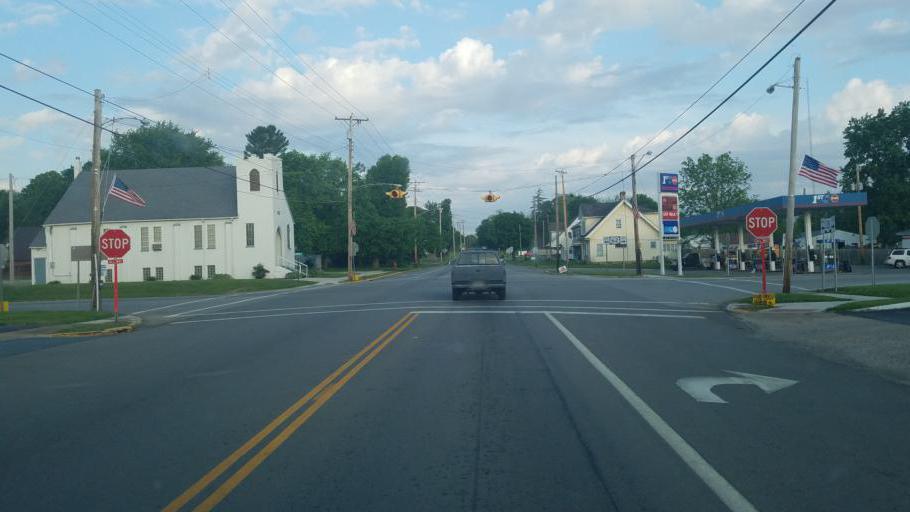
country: US
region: Ohio
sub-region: Highland County
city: Leesburg
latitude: 39.3457
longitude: -83.5594
